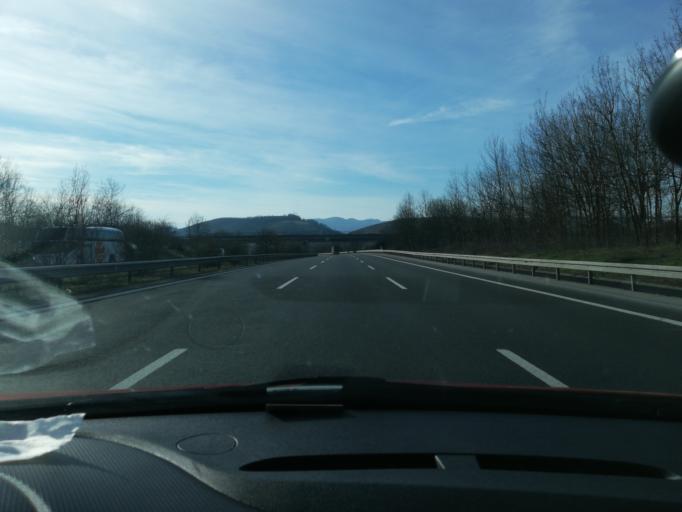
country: TR
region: Duzce
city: Gumusova
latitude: 40.8411
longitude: 30.9806
